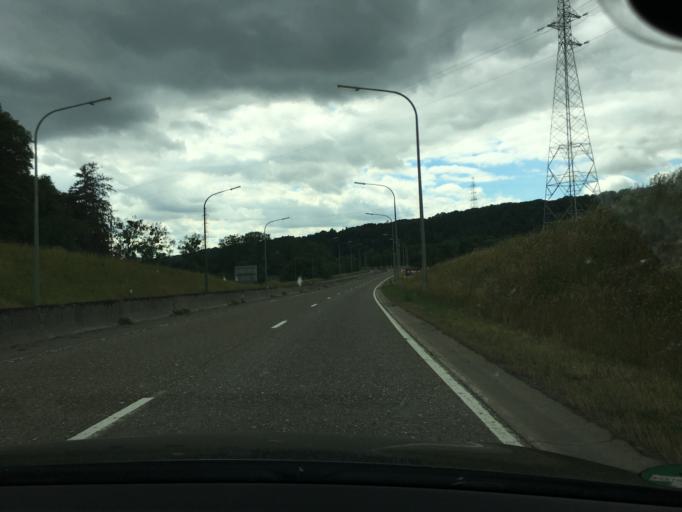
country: BE
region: Wallonia
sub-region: Province de Liege
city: Amay
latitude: 50.5553
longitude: 5.3446
